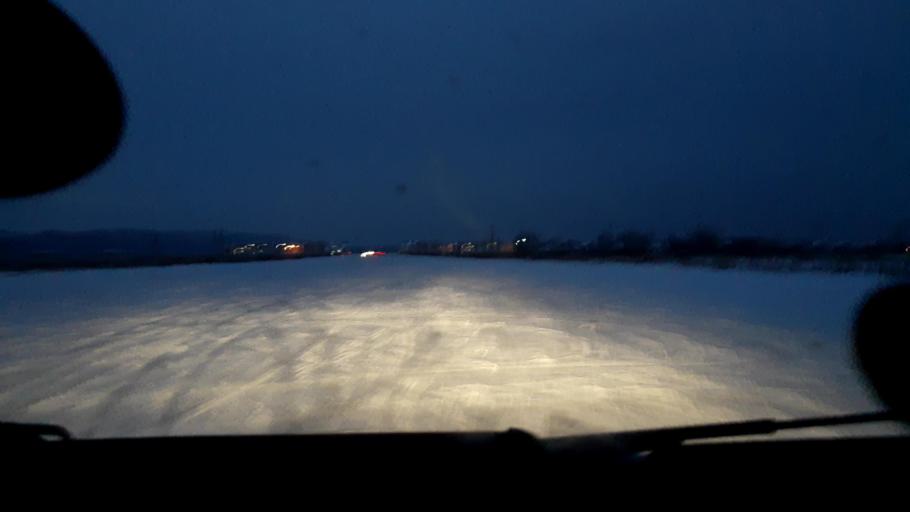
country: RU
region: Bashkortostan
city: Ufa
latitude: 54.8270
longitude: 56.1647
